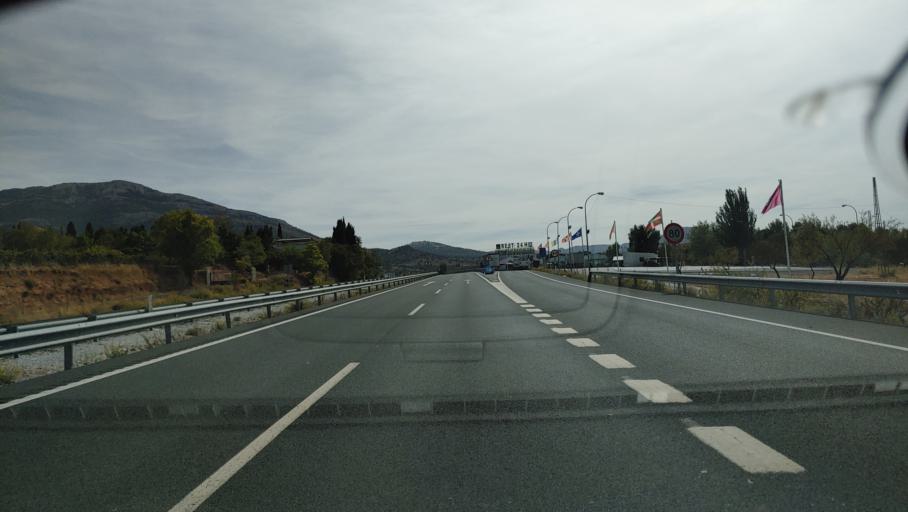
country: ES
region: Andalusia
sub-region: Provincia de Granada
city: Gor
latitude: 37.4164
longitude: -2.9184
